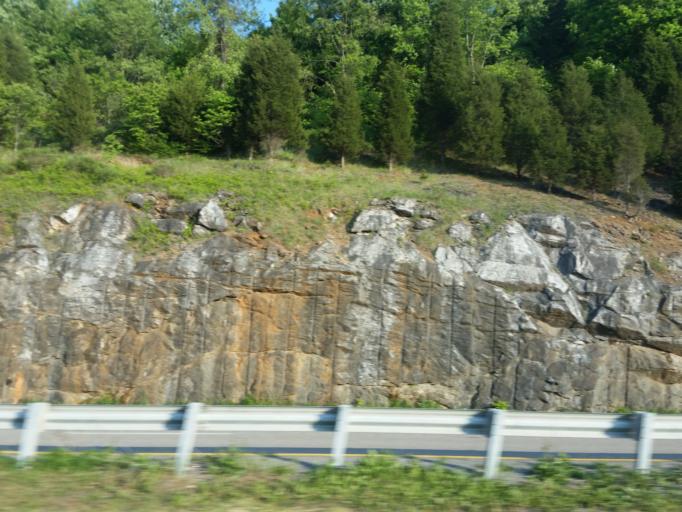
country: US
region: Virginia
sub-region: Russell County
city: Lebanon
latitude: 36.8879
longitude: -82.1011
